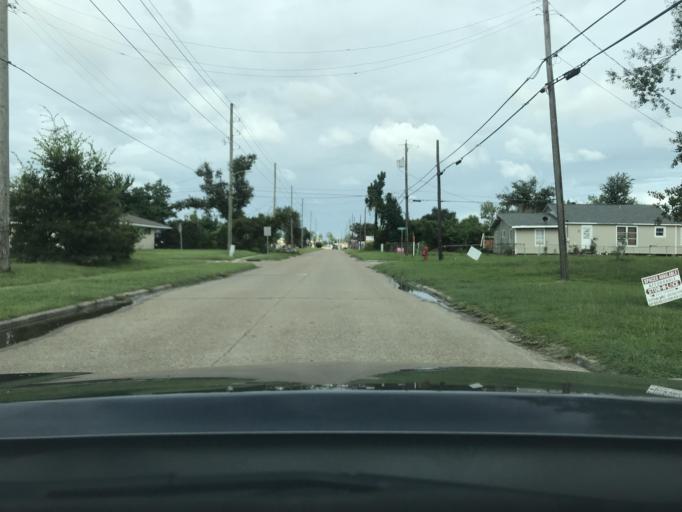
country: US
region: Louisiana
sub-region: Calcasieu Parish
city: Westlake
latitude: 30.2477
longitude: -93.2638
